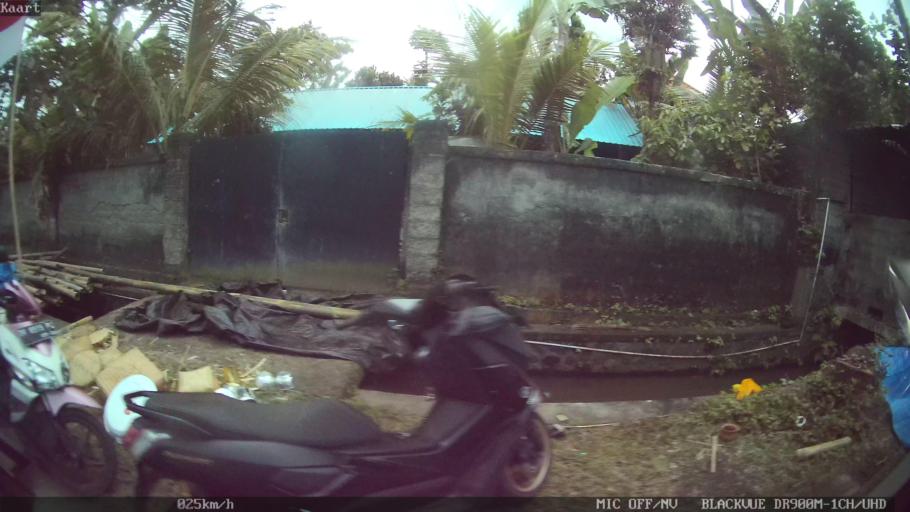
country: ID
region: Bali
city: Banjar Petak
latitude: -8.4394
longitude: 115.3235
